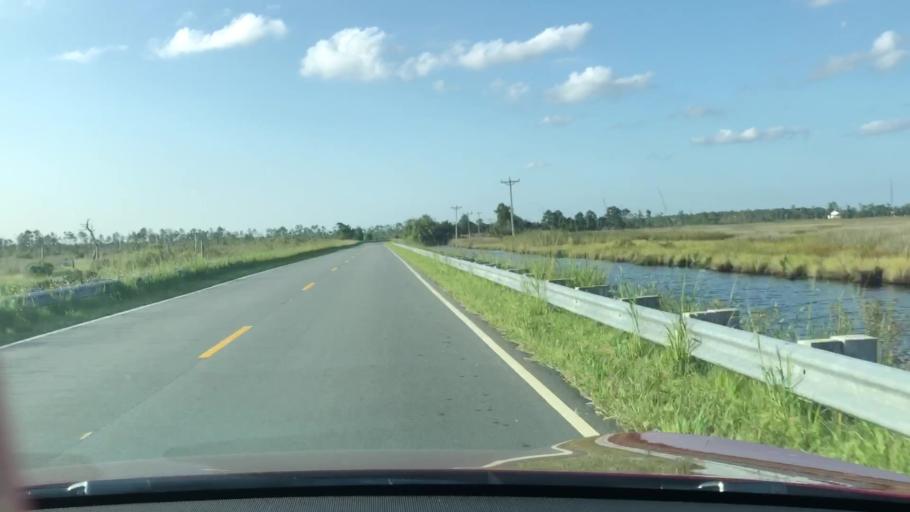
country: US
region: North Carolina
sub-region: Dare County
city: Wanchese
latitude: 35.6870
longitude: -75.7807
